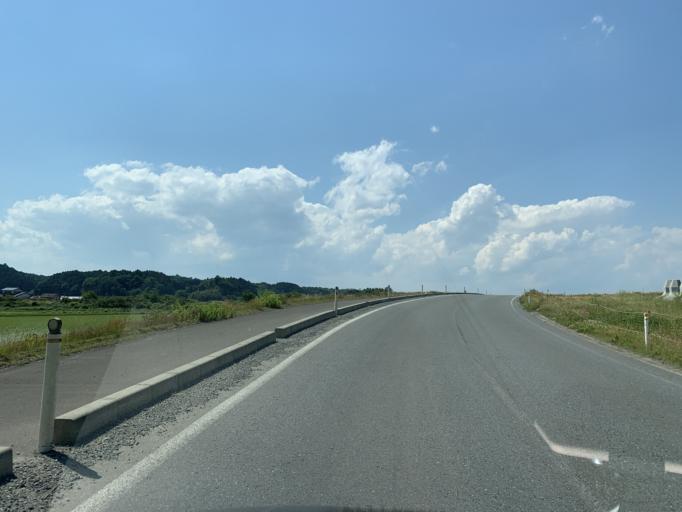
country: JP
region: Miyagi
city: Yamoto
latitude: 38.3879
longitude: 141.1621
